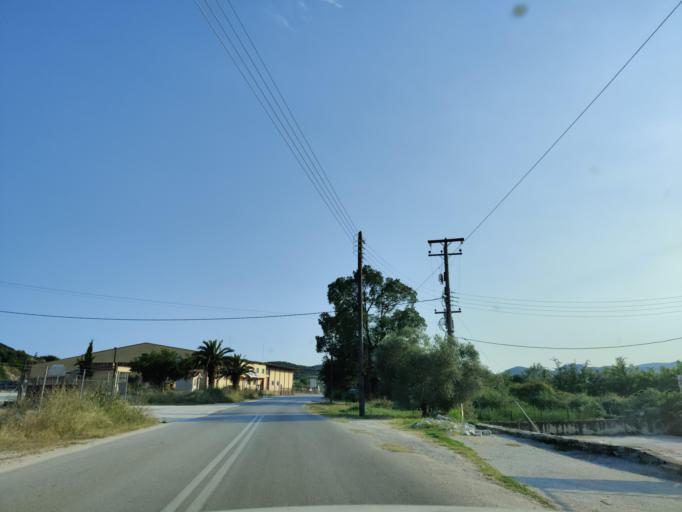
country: GR
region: East Macedonia and Thrace
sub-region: Nomos Kavalas
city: Nea Peramos
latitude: 40.8251
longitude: 24.2879
